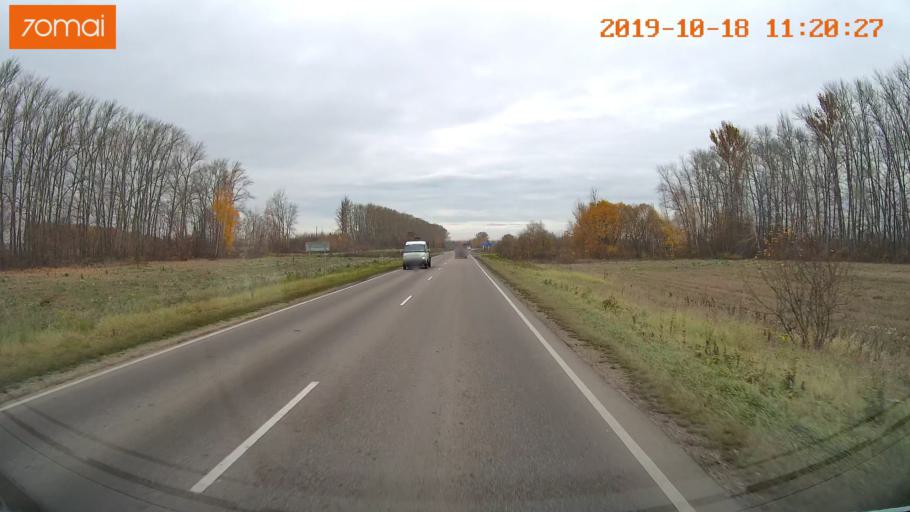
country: RU
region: Tula
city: Kimovsk
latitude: 54.0610
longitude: 38.5586
